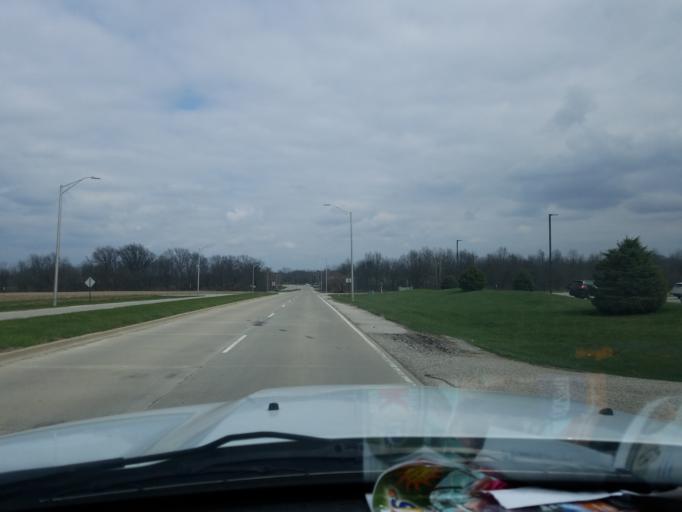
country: US
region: Indiana
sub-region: Sullivan County
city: Farmersburg
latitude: 39.3426
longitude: -87.3964
